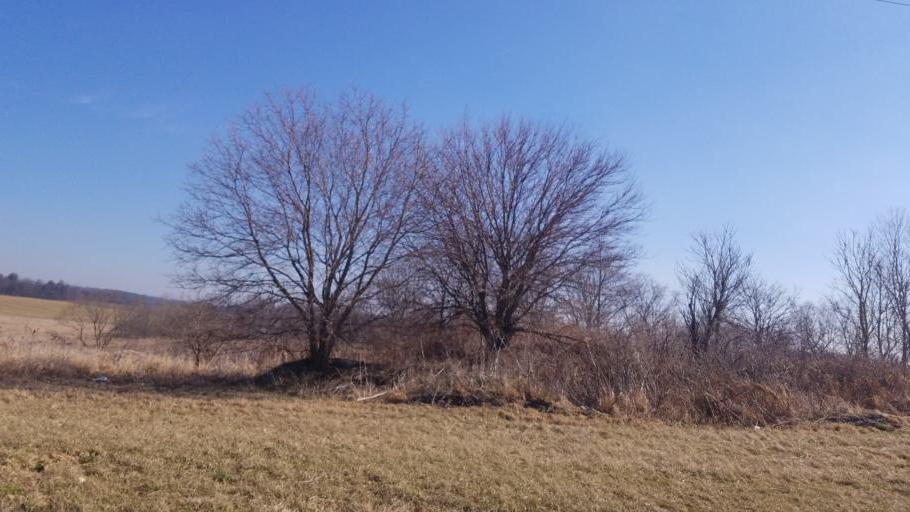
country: US
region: Ohio
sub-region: Richland County
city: Shelby
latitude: 40.9263
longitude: -82.5805
